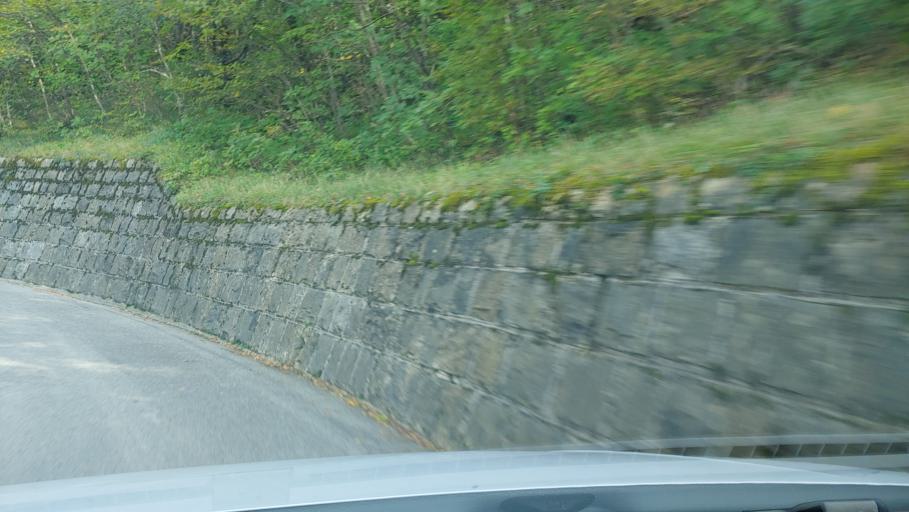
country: SI
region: Ajdovscina
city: Ajdovscina
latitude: 45.9016
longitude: 13.9103
